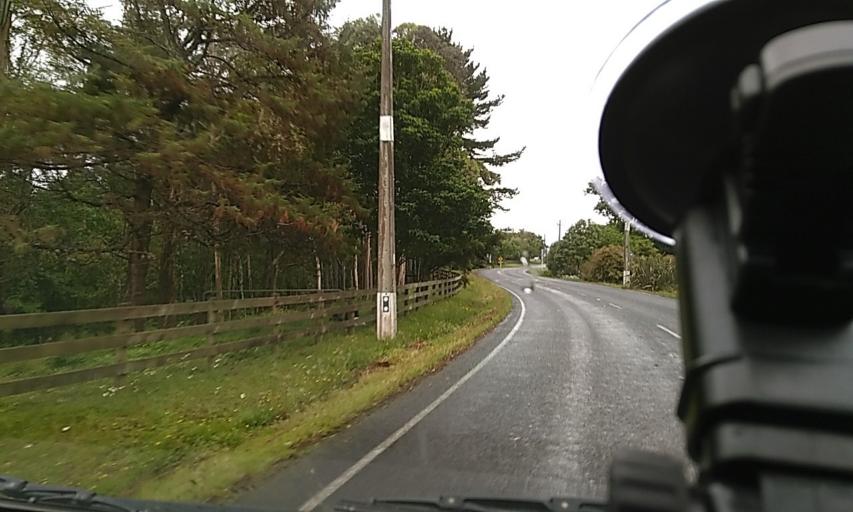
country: NZ
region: Auckland
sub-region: Auckland
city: Pukekohe East
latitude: -37.3249
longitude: 174.9176
